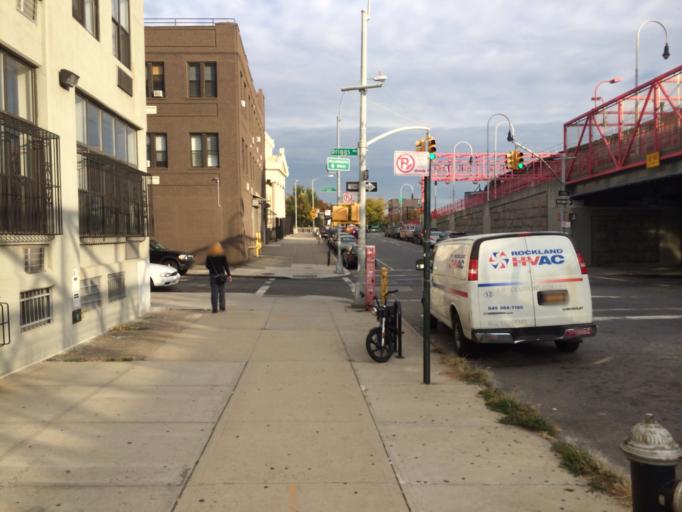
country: US
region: New York
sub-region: Queens County
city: Long Island City
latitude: 40.7109
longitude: -73.9621
